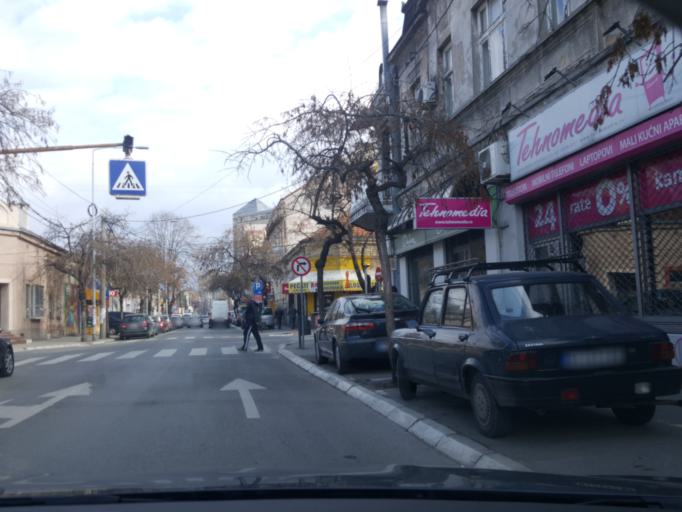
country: RS
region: Central Serbia
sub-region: Nisavski Okrug
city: Nis
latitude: 43.3172
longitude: 21.8975
